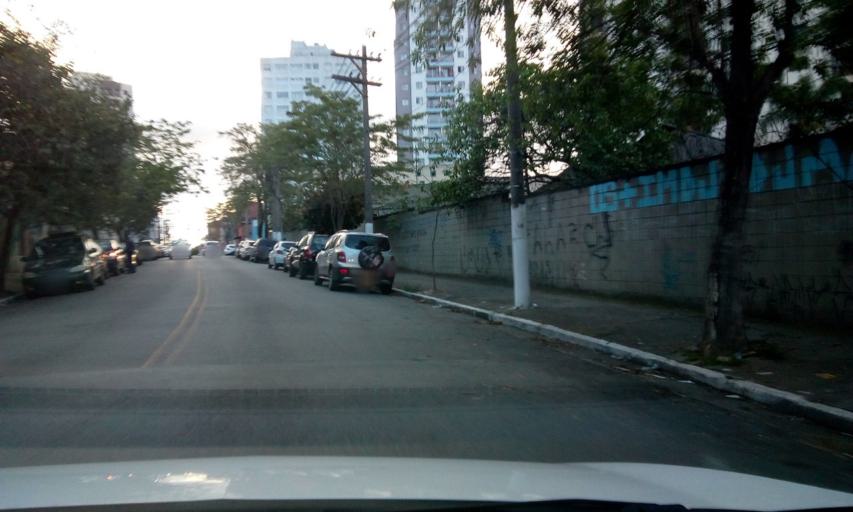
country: BR
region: Sao Paulo
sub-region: Sao Paulo
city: Sao Paulo
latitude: -23.5386
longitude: -46.5939
